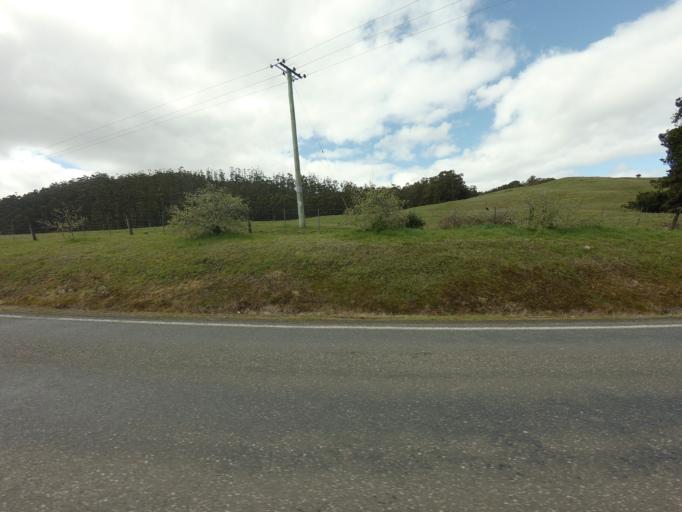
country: AU
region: Tasmania
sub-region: Huon Valley
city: Cygnet
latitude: -43.2848
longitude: 147.0111
